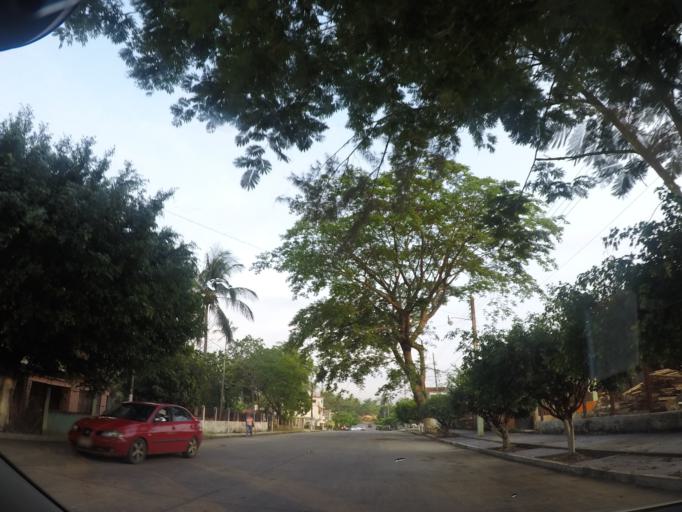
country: MX
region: Oaxaca
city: Matias Romero
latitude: 16.8740
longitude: -95.0426
